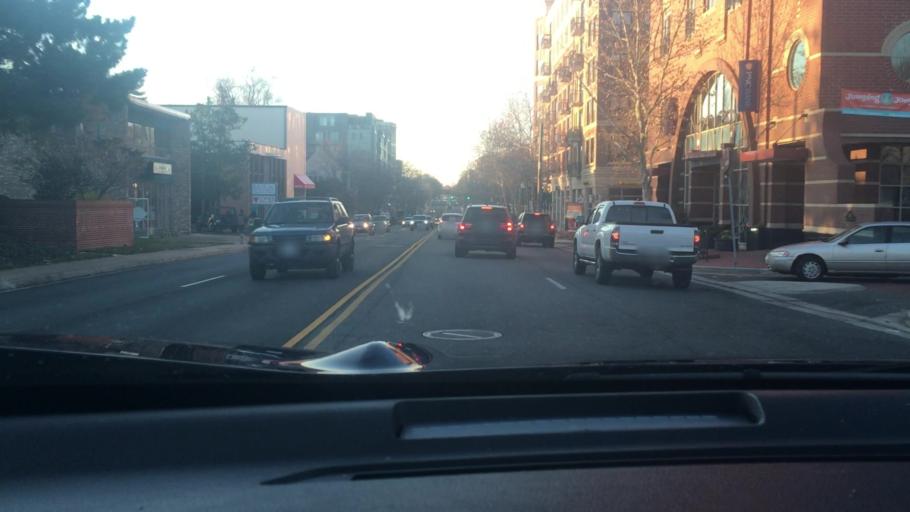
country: US
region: Virginia
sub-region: City of Falls Church
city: Falls Church
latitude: 38.8855
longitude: -77.1761
